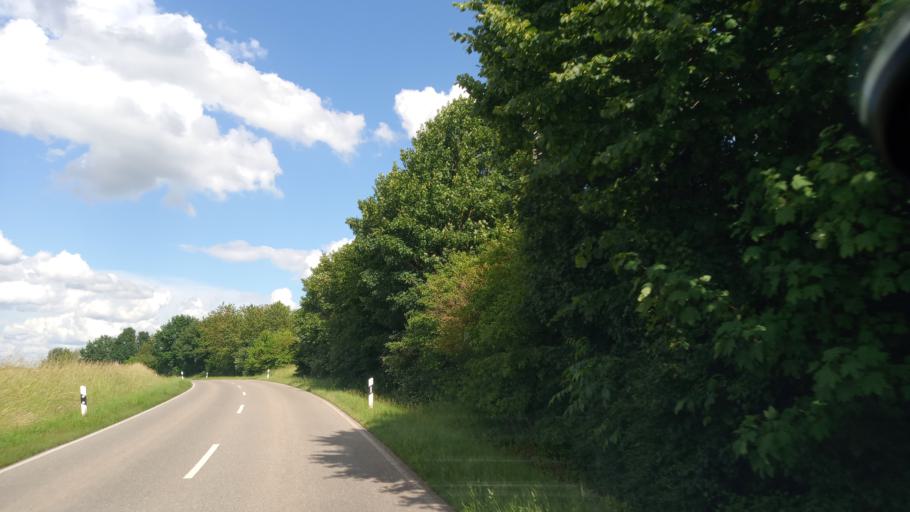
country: DE
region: Bavaria
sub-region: Upper Bavaria
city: Rohrmoos
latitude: 48.3558
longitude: 11.4342
